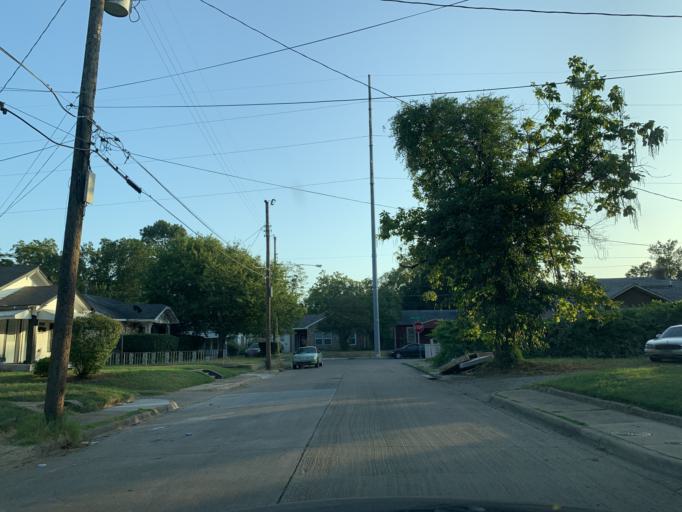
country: US
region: Texas
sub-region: Dallas County
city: Dallas
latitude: 32.7530
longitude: -96.7486
